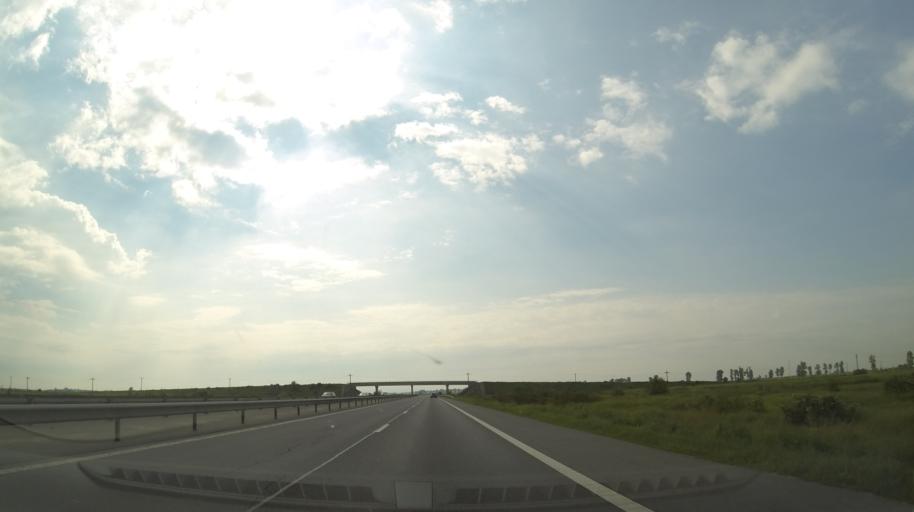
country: RO
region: Dambovita
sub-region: Comuna Corbii Mari
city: Corbii Mari
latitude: 44.5472
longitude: 25.5089
